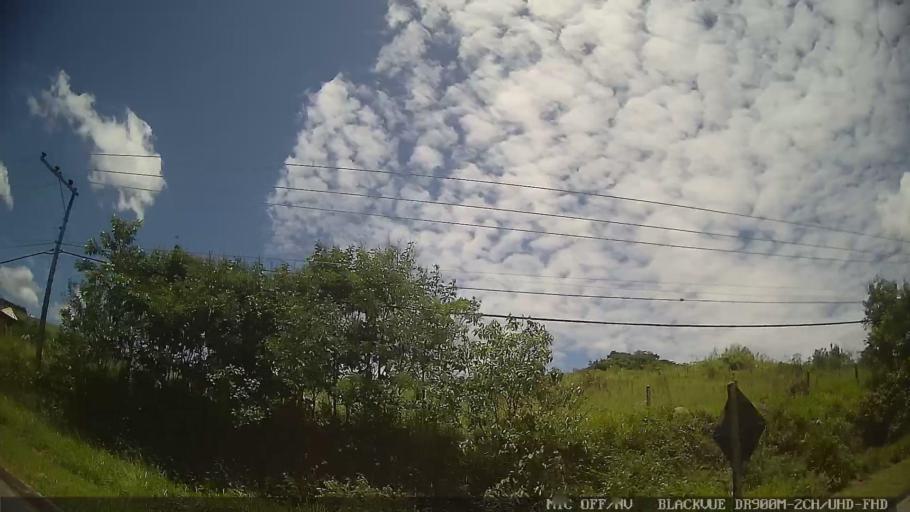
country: BR
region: Sao Paulo
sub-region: Santa Branca
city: Santa Branca
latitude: -23.5234
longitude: -45.8859
